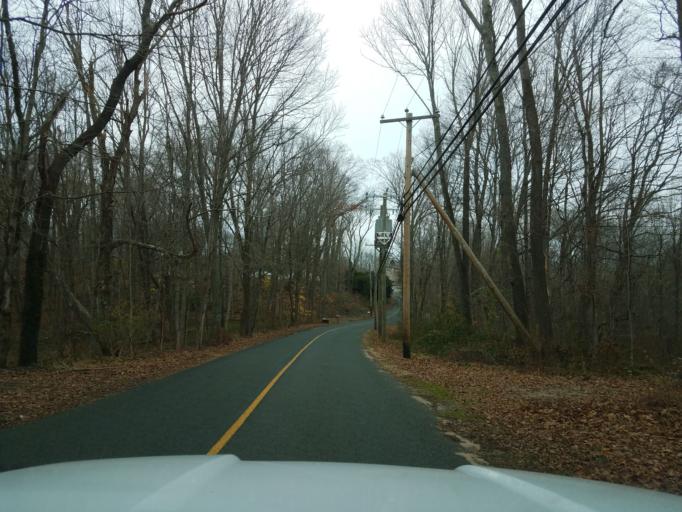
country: US
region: Connecticut
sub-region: New Haven County
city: North Branford
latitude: 41.3517
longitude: -72.7289
